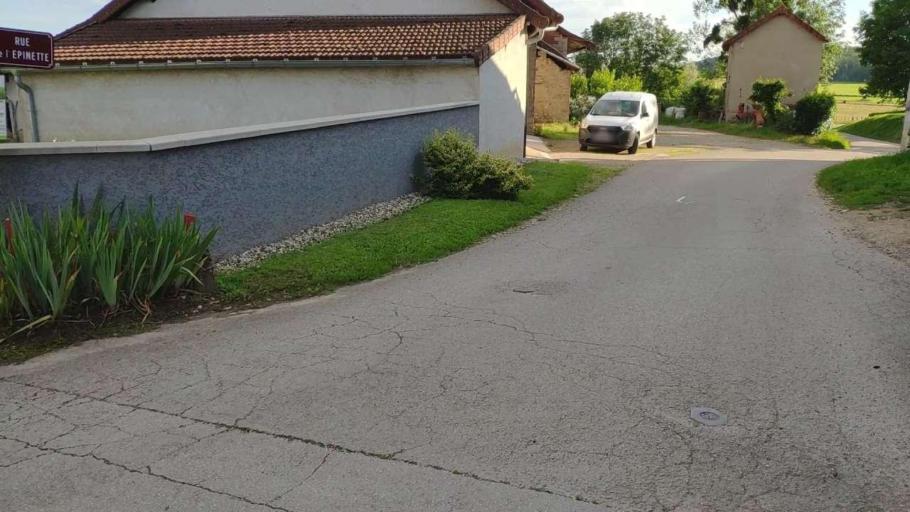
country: FR
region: Franche-Comte
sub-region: Departement du Jura
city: Bletterans
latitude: 46.7806
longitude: 5.4929
